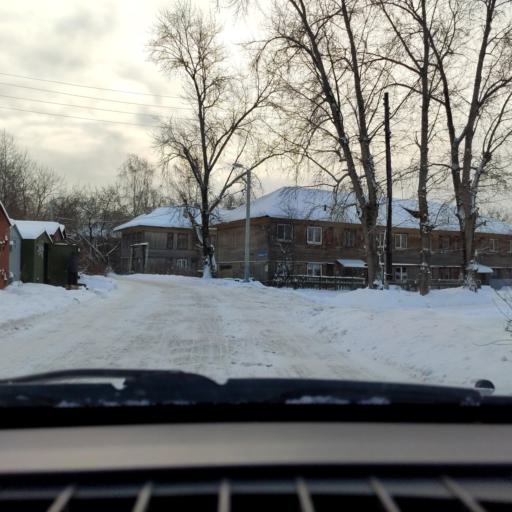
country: RU
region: Perm
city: Kondratovo
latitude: 58.0077
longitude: 56.1217
